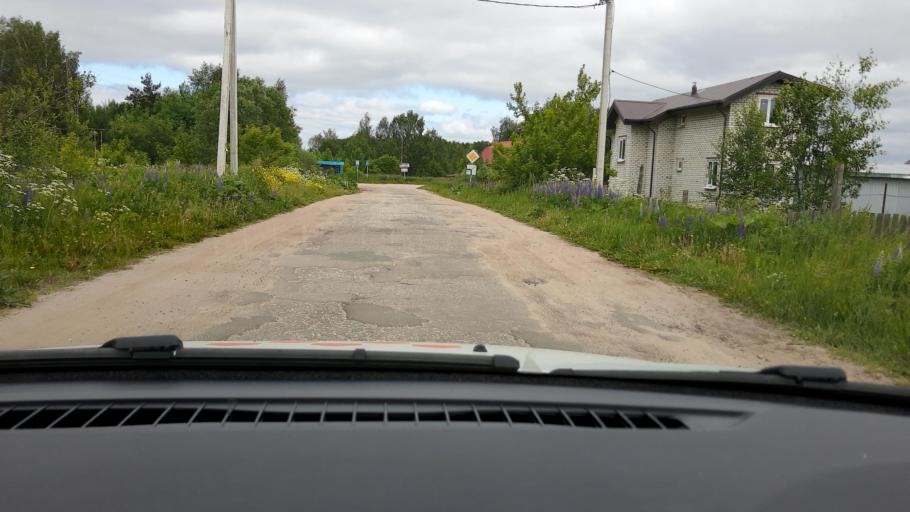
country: RU
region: Nizjnij Novgorod
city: Sitniki
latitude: 56.5213
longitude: 44.1089
